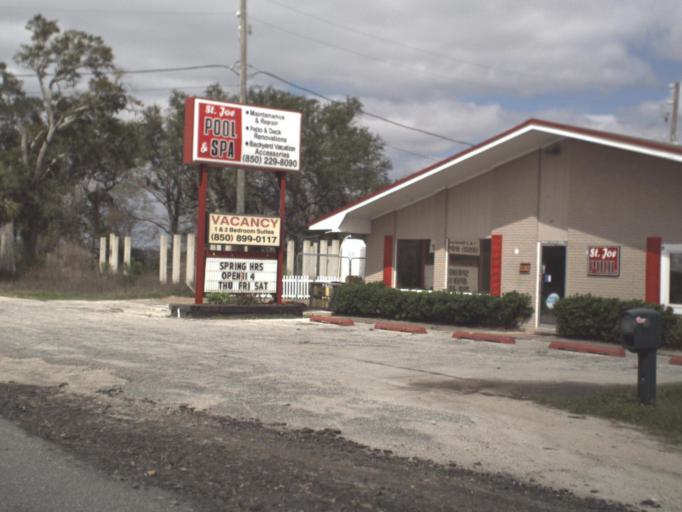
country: US
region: Florida
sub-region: Franklin County
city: Eastpoint
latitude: 29.7357
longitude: -84.8997
